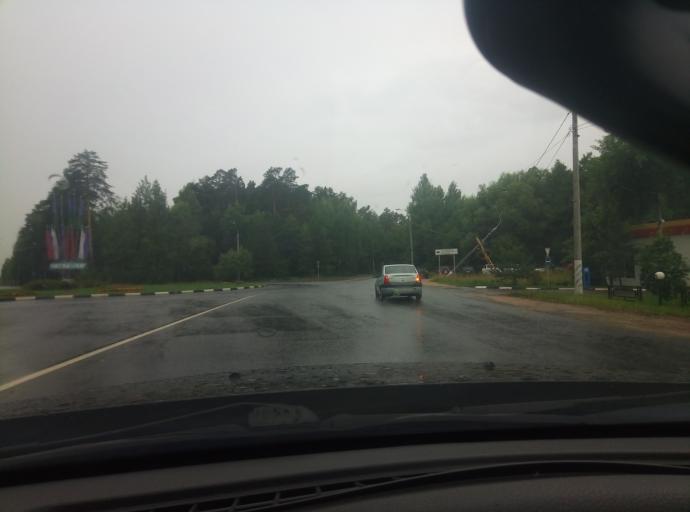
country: RU
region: Moskovskaya
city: Protvino
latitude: 54.8802
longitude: 37.2383
